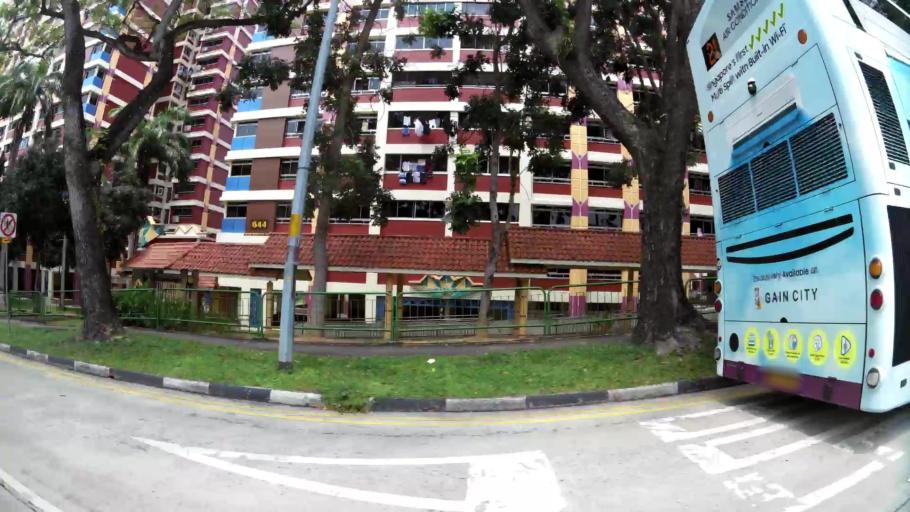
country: SG
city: Singapore
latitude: 1.3305
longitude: 103.9057
